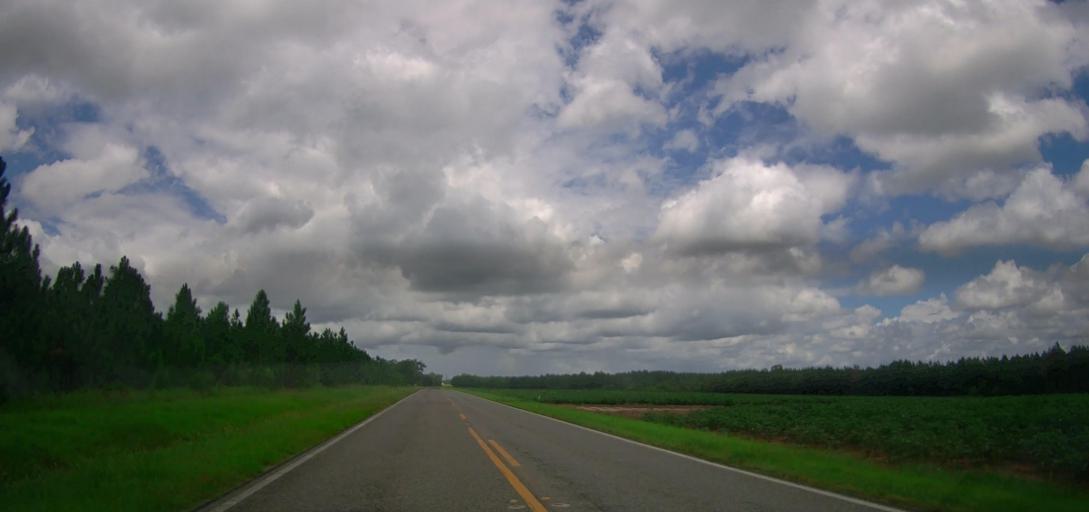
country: US
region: Georgia
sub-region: Wilcox County
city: Rochelle
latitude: 31.8771
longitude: -83.5580
